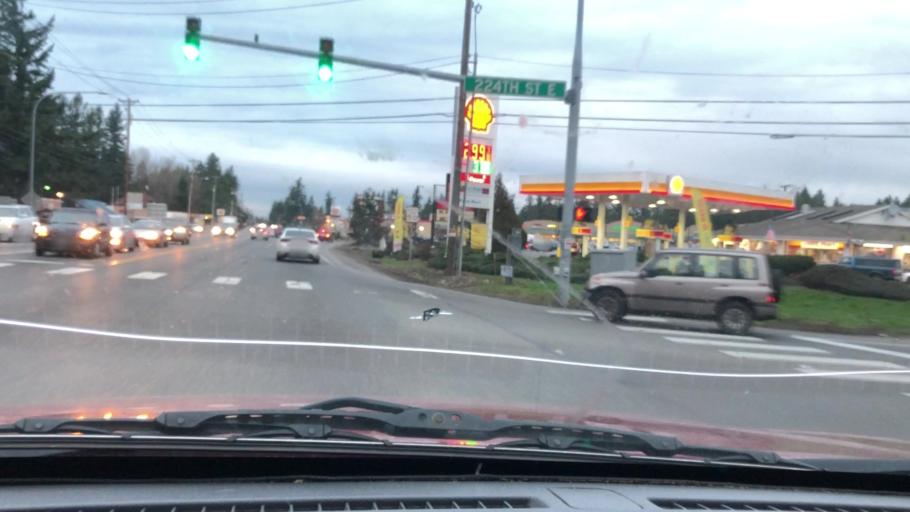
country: US
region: Washington
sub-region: Pierce County
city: Elk Plain
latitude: 47.0531
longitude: -122.3977
